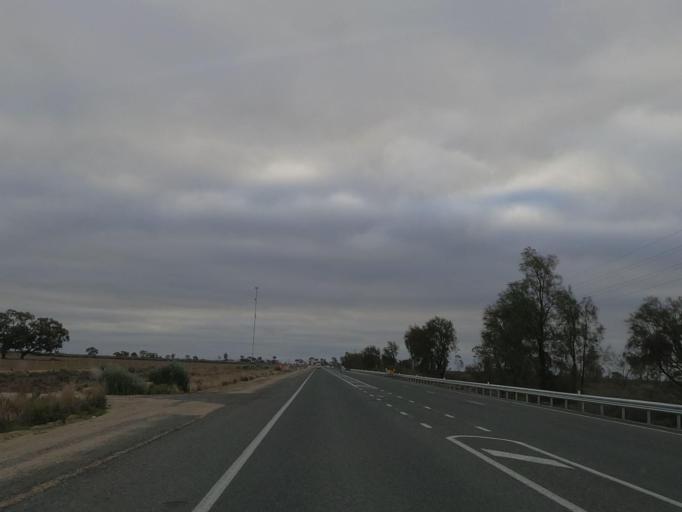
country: AU
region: Victoria
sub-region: Swan Hill
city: Swan Hill
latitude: -35.5323
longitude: 143.7417
